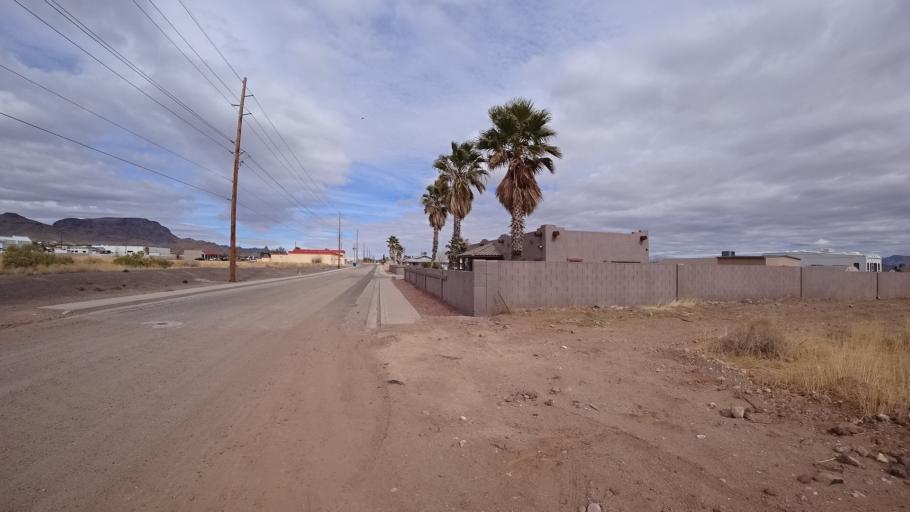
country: US
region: Arizona
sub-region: Mohave County
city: New Kingman-Butler
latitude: 35.2302
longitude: -114.0336
